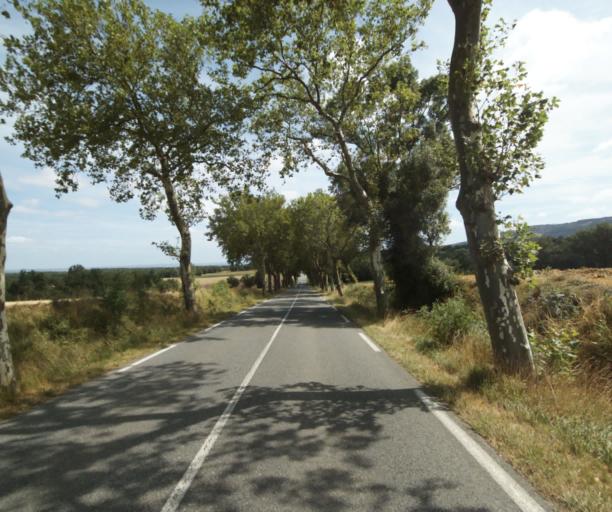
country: FR
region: Midi-Pyrenees
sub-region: Departement du Tarn
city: Soreze
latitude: 43.4683
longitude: 2.0984
